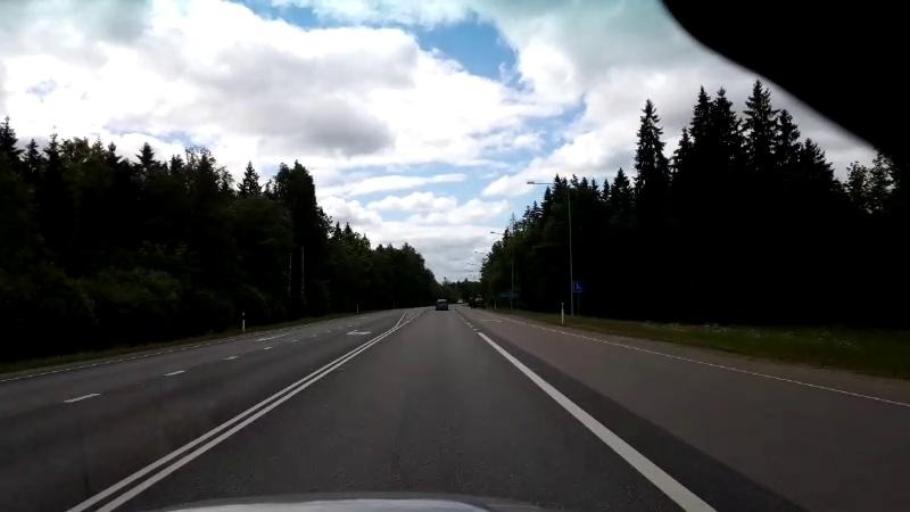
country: EE
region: Paernumaa
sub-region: Halinga vald
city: Parnu-Jaagupi
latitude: 58.6161
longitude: 24.5125
